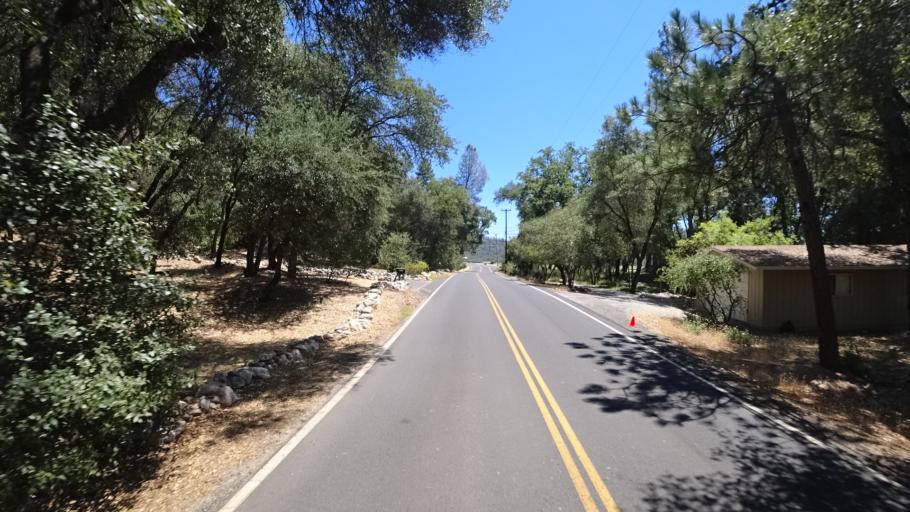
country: US
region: California
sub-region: Calaveras County
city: Murphys
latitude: 38.1294
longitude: -120.4434
